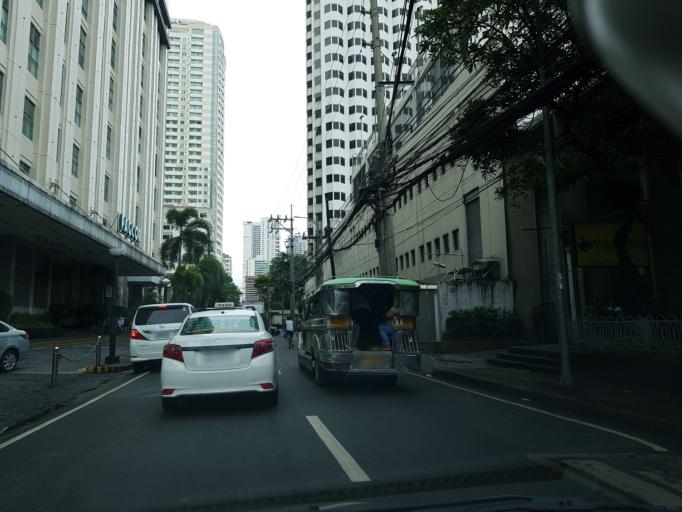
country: PH
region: Metro Manila
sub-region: City of Manila
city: Port Area
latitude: 14.5735
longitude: 120.9822
